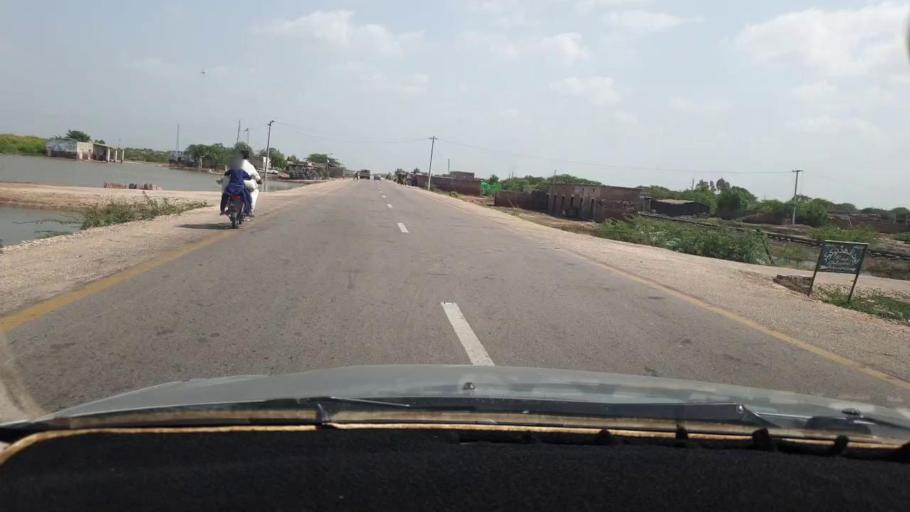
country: PK
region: Sindh
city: Digri
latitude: 25.1201
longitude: 69.1510
